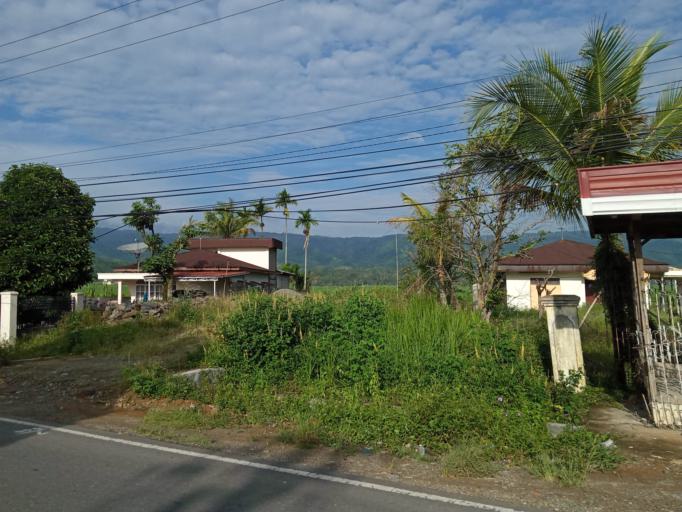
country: ID
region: Jambi
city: Semurup
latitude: -2.0041
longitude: 101.3768
